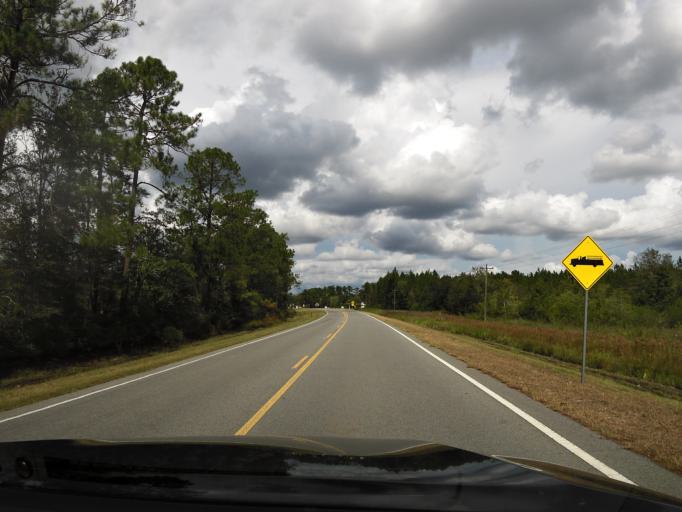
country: US
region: Georgia
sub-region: Brantley County
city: Nahunta
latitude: 31.1459
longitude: -81.9921
